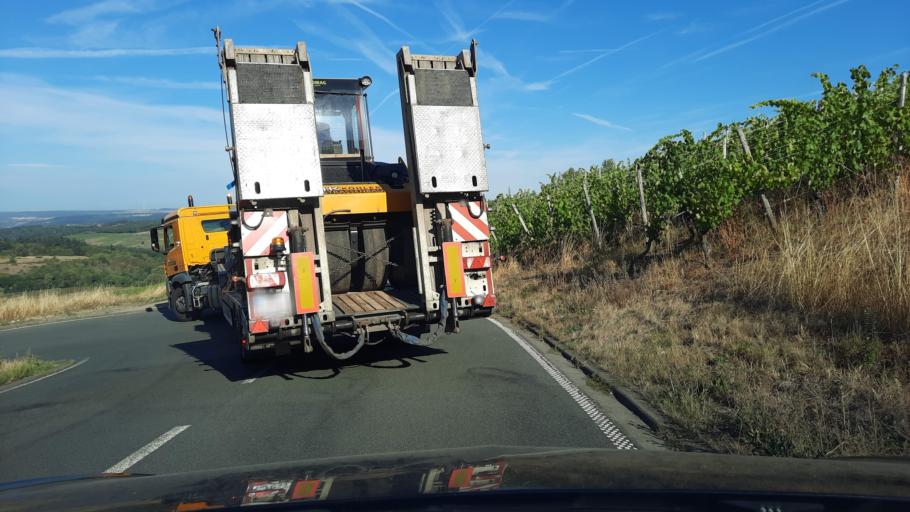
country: DE
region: Rheinland-Pfalz
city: Pellingen
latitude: 49.6835
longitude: 6.6480
